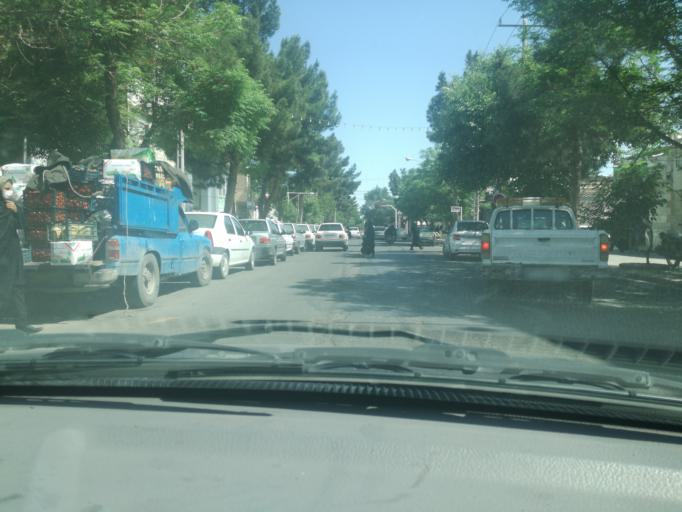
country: IR
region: Razavi Khorasan
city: Sarakhs
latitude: 36.5358
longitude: 61.1631
